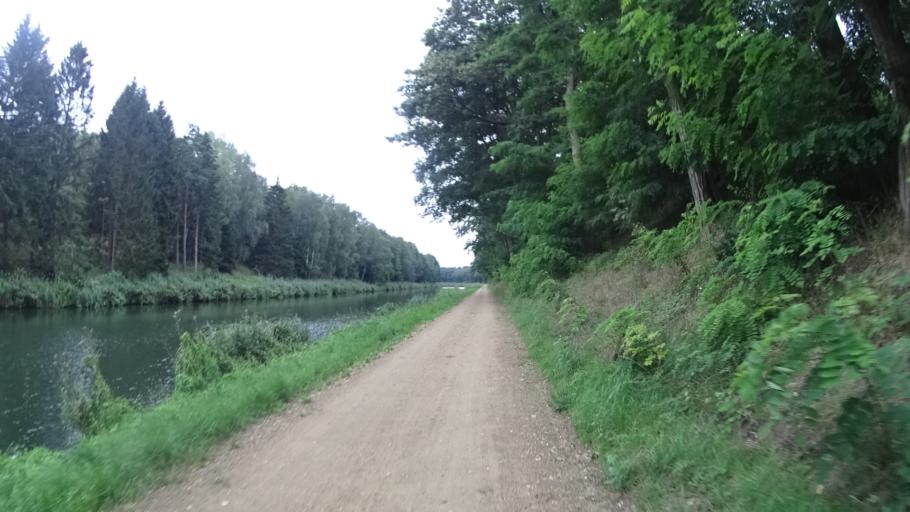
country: DE
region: Schleswig-Holstein
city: Grambek
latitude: 53.5924
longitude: 10.6658
